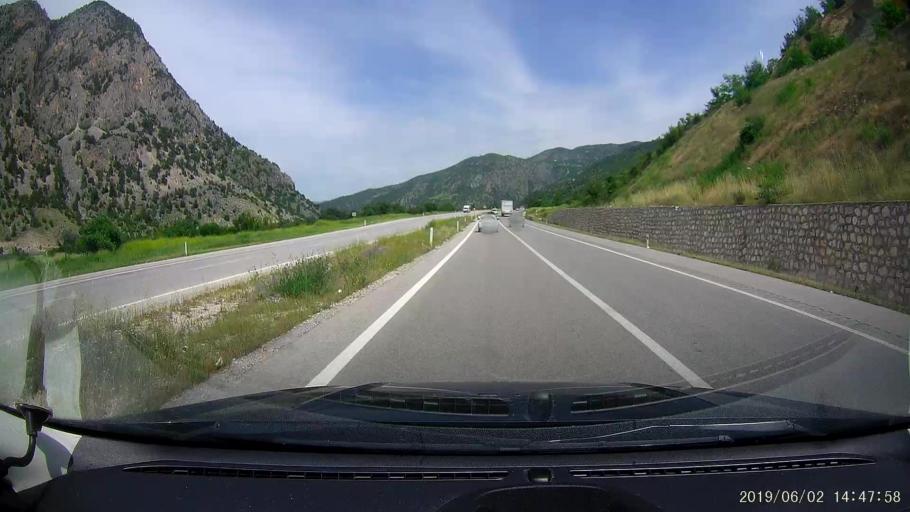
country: TR
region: Corum
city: Hacihamza
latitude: 41.0654
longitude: 34.4704
